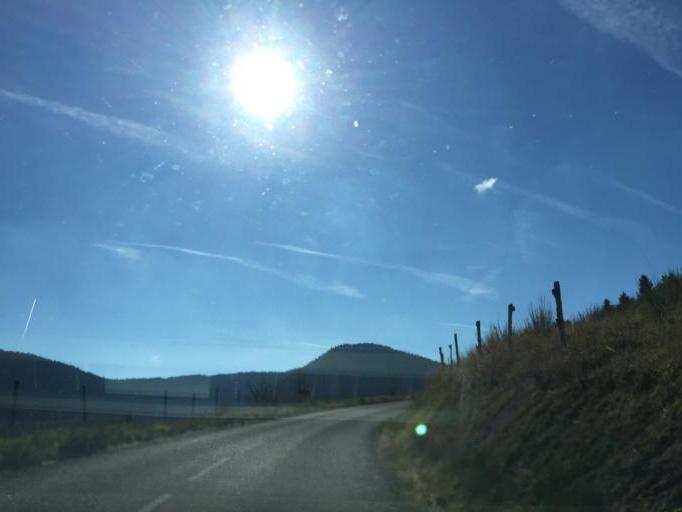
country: FR
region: Rhone-Alpes
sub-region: Departement de la Loire
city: Saint-Chamond
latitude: 45.3933
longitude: 4.5388
